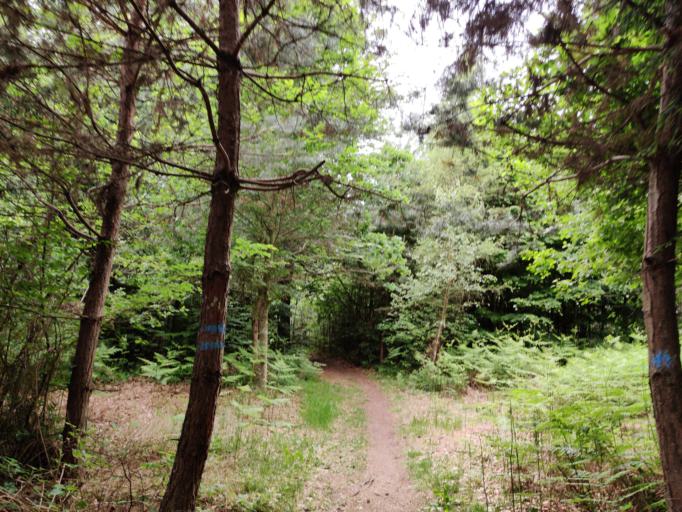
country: AT
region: Carinthia
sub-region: Klagenfurt am Woerthersee
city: Klagenfurt am Woerthersee
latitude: 46.6306
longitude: 14.2465
